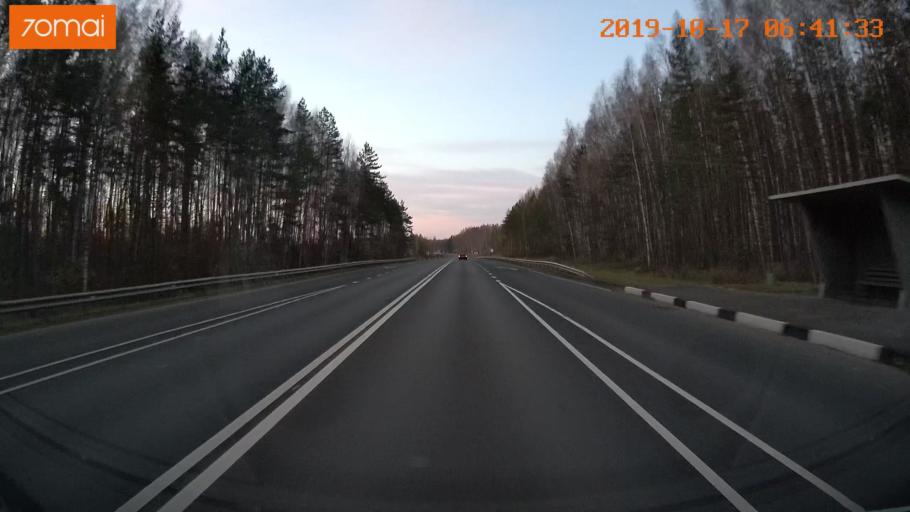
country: RU
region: Ivanovo
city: Nerl'
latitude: 56.6135
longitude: 40.5592
